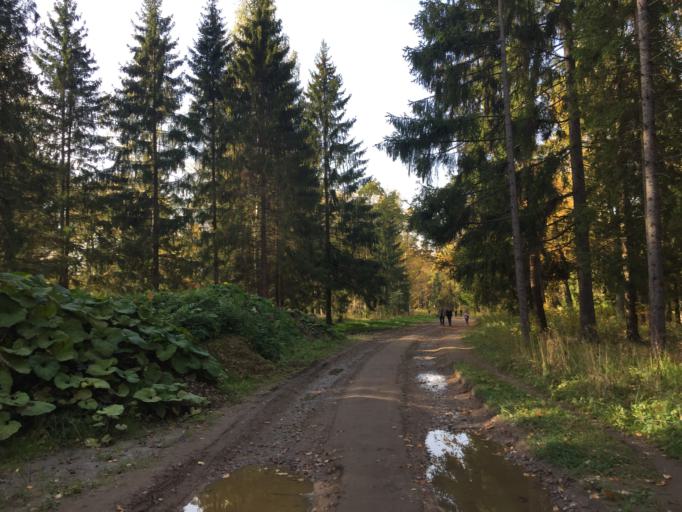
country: RU
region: St.-Petersburg
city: Pushkin
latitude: 59.7163
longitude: 30.3779
